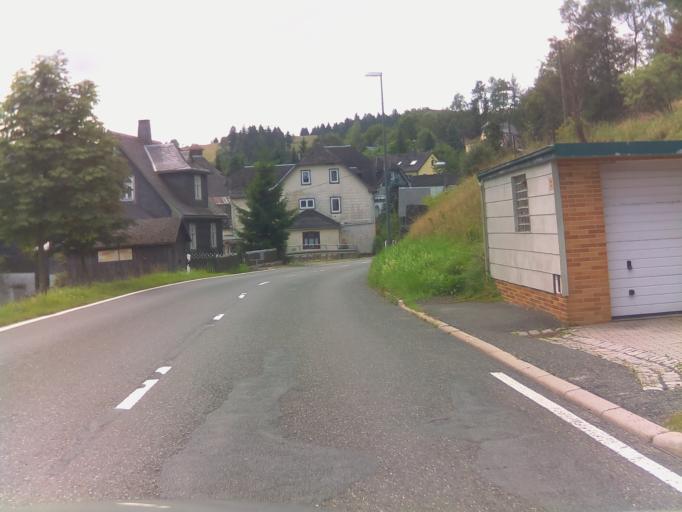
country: DE
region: Bavaria
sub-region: Upper Franconia
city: Tettau
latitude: 50.4741
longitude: 11.2601
